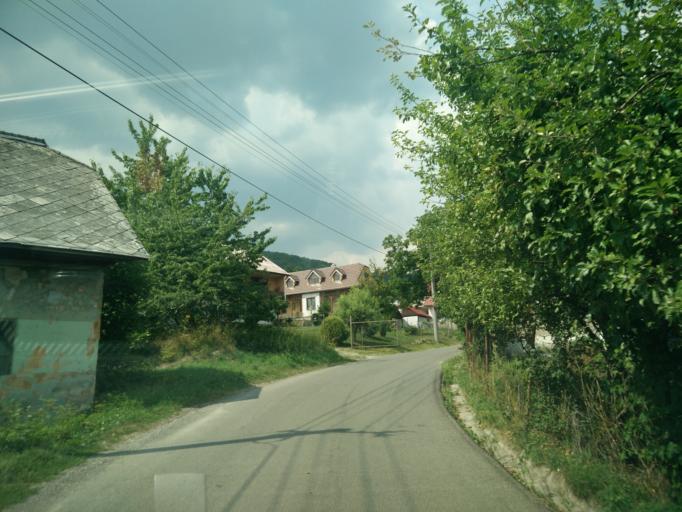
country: SK
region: Nitriansky
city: Handlova
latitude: 48.6142
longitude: 18.7065
